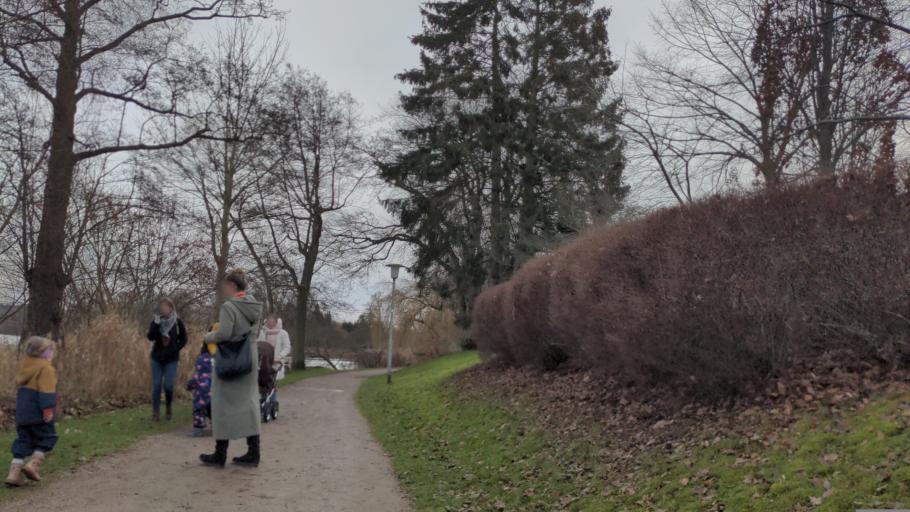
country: DE
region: Schleswig-Holstein
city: Malente
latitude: 54.1715
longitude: 10.5670
